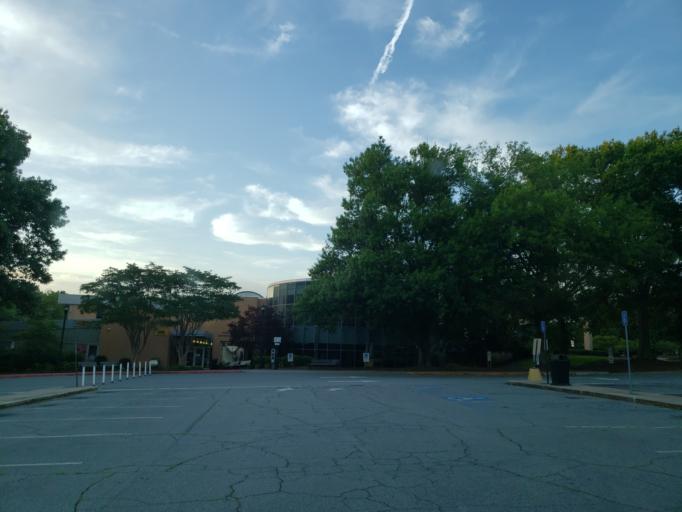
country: US
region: Georgia
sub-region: Cobb County
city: Kennesaw
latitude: 34.0374
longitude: -84.5830
